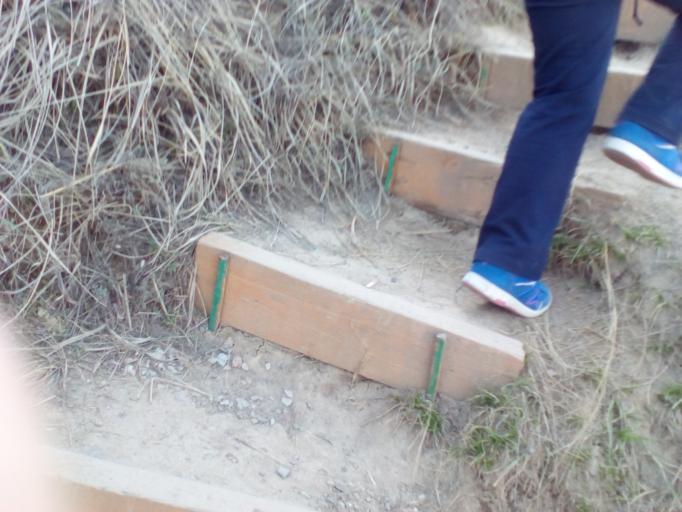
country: KZ
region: Almaty Oblysy
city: Burunday
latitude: 43.1527
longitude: 76.5689
